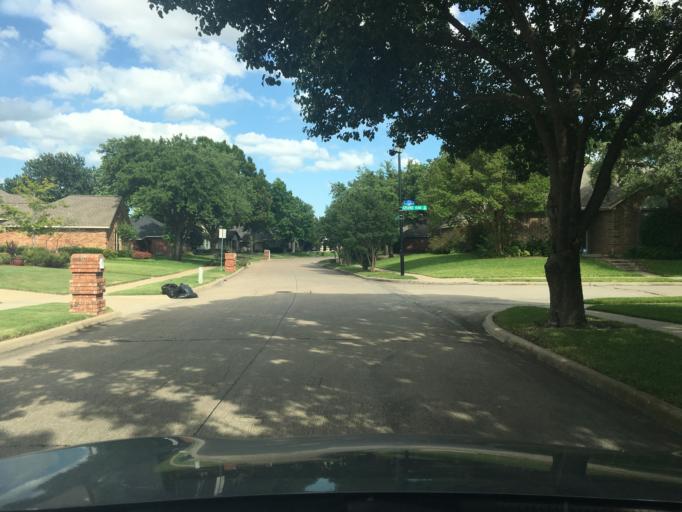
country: US
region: Texas
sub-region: Dallas County
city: Garland
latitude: 32.9338
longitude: -96.6717
